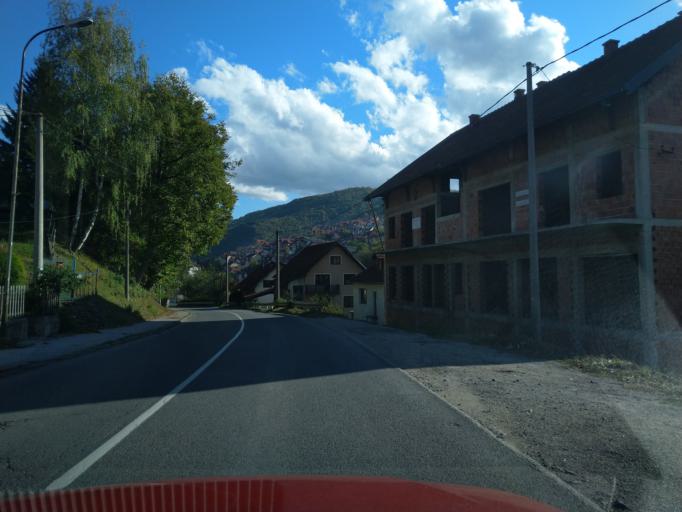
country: RS
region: Central Serbia
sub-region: Zlatiborski Okrug
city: Uzice
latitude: 43.8621
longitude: 19.8256
